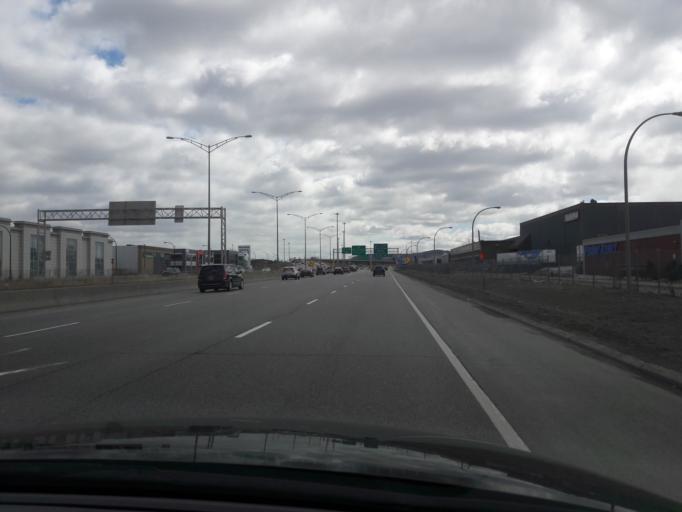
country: CA
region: Quebec
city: Mont-Royal
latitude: 45.5290
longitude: -73.6597
